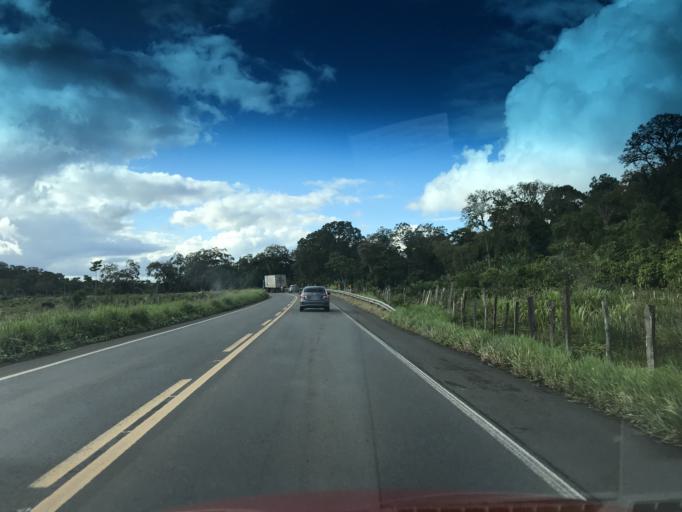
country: BR
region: Bahia
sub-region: Ibirapitanga
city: Ibirapitanga
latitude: -14.1571
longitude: -39.3270
